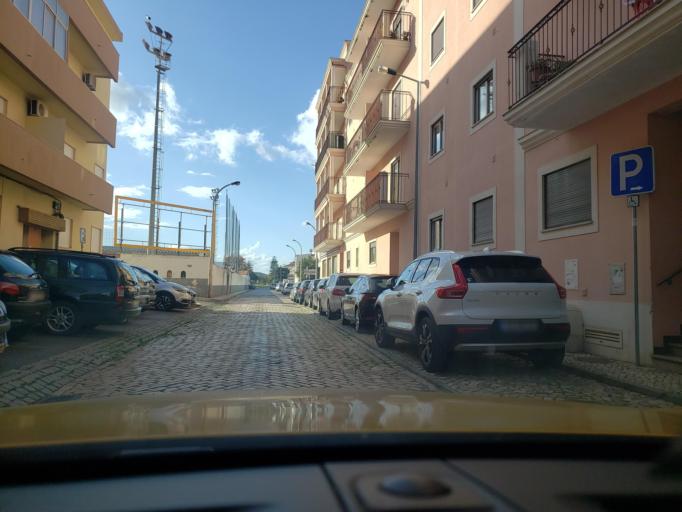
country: PT
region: Faro
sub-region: Silves
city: Silves
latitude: 37.1869
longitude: -8.4415
